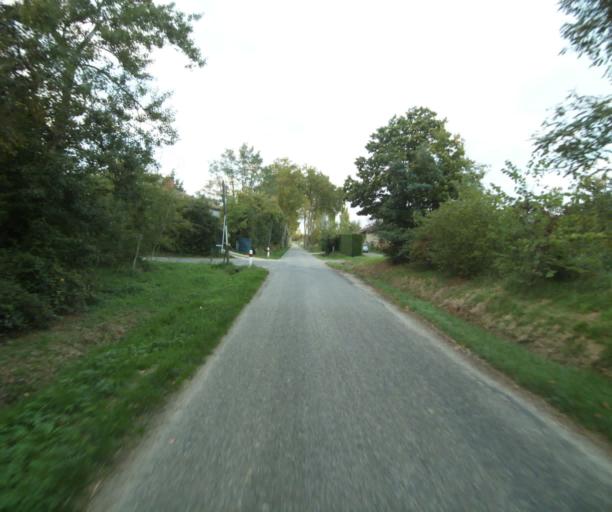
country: FR
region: Aquitaine
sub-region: Departement des Landes
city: Gabarret
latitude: 43.9750
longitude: 0.0935
